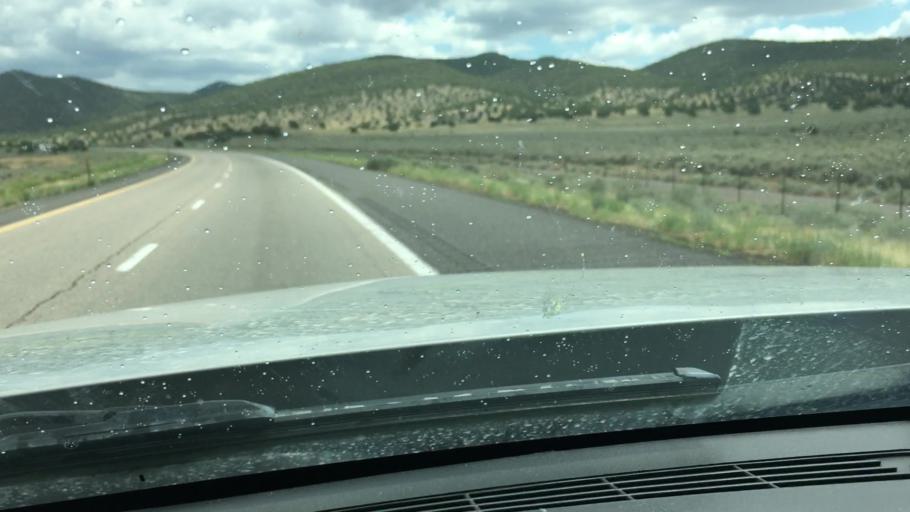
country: US
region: Utah
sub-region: Beaver County
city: Beaver
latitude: 38.1960
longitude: -112.6462
